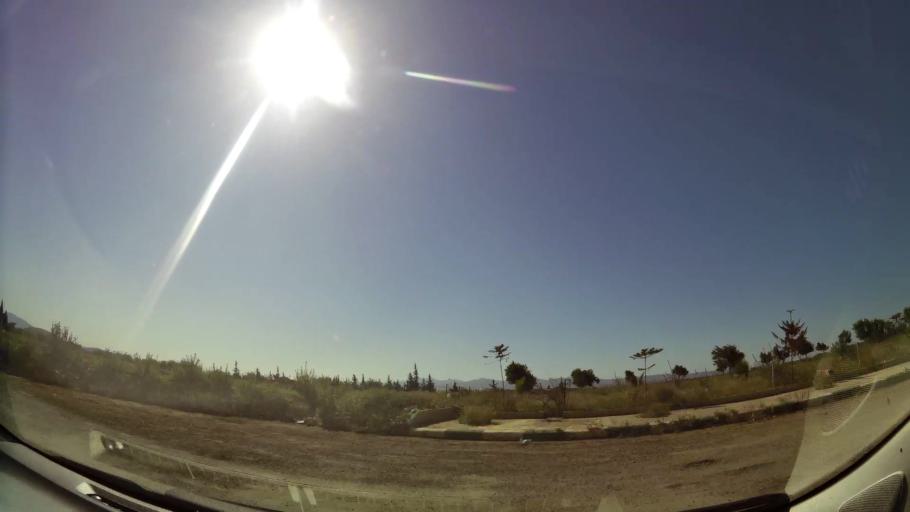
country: MA
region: Oriental
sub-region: Berkane-Taourirt
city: Berkane
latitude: 34.9413
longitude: -2.3428
